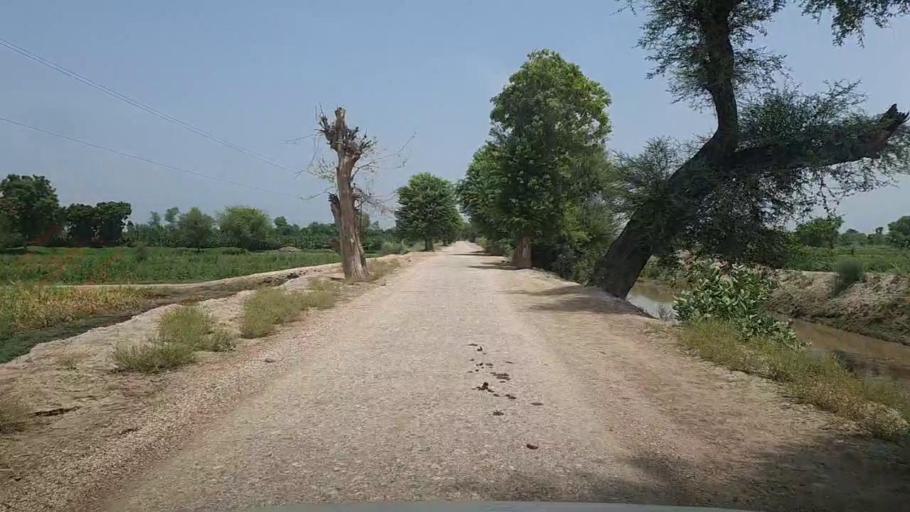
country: PK
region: Sindh
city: Karaundi
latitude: 26.9065
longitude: 68.3325
